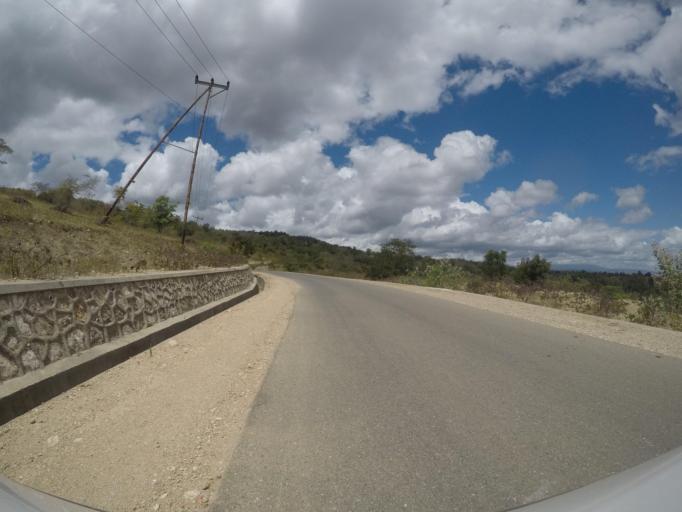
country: TL
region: Lautem
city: Lospalos
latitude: -8.3633
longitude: 126.9285
